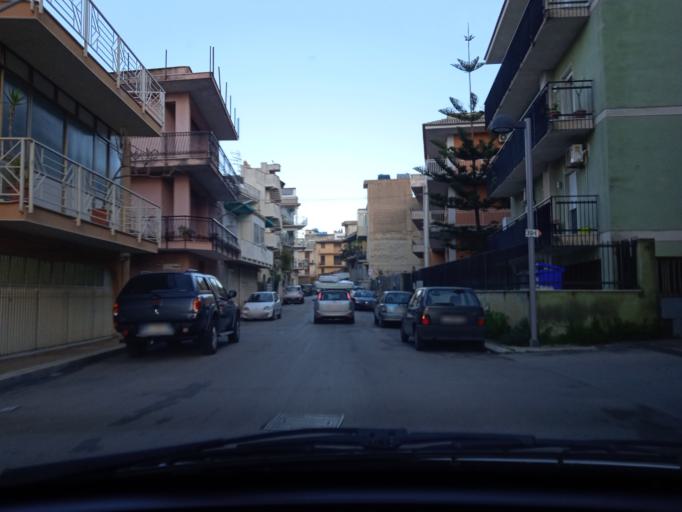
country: IT
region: Sicily
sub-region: Palermo
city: Villabate
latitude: 38.0737
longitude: 13.4456
